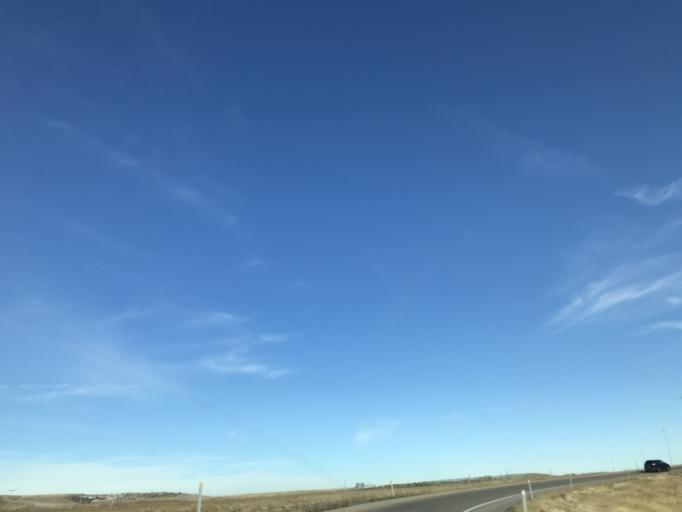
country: US
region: Colorado
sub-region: Adams County
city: Aurora
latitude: 39.8358
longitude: -104.7491
